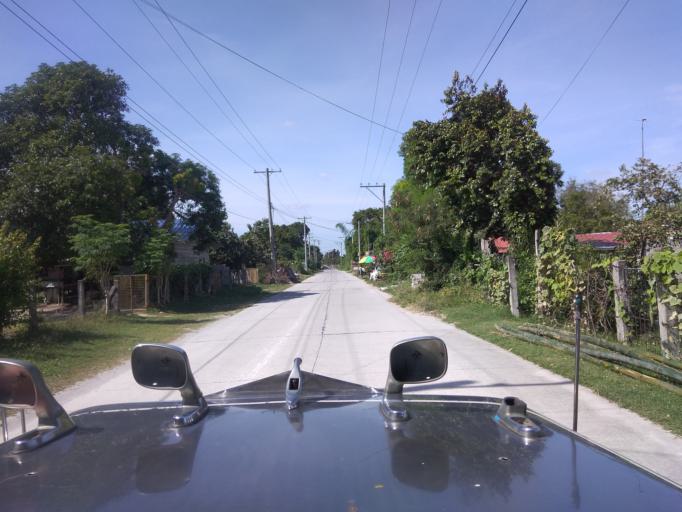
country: PH
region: Central Luzon
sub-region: Province of Pampanga
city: Magliman
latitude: 15.0253
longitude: 120.6527
